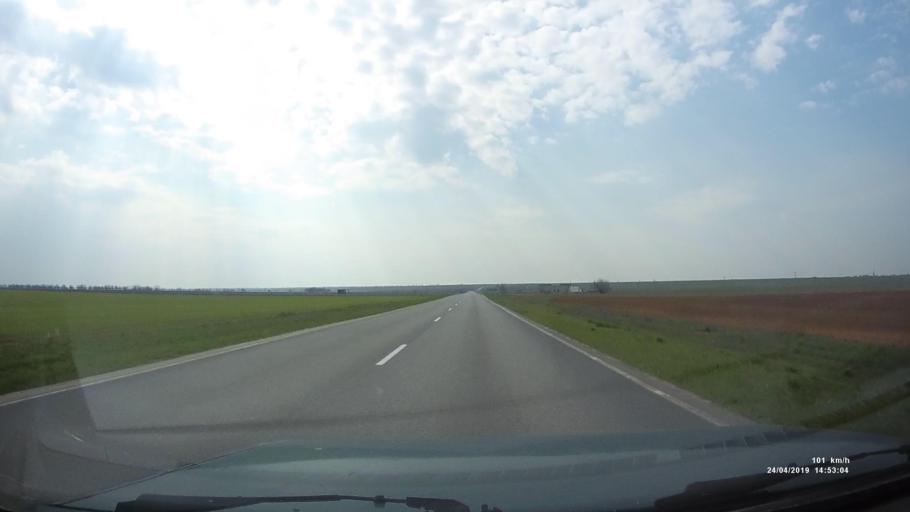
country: RU
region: Rostov
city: Remontnoye
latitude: 46.5310
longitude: 43.6671
